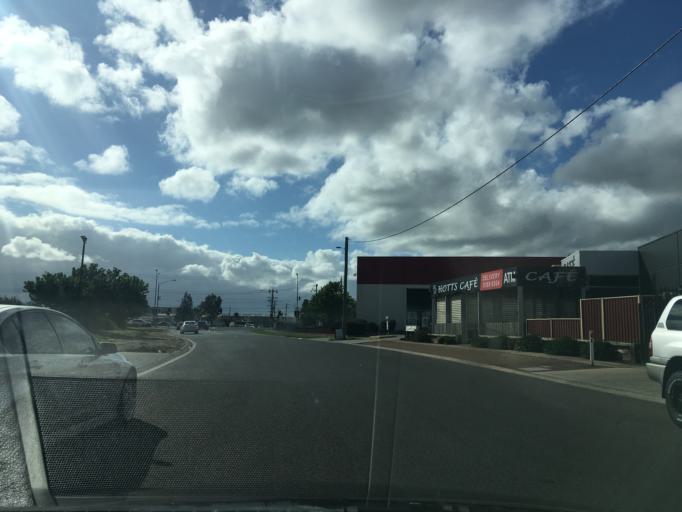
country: AU
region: Victoria
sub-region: Wyndham
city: Williams Landing
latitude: -37.8729
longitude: 144.7264
